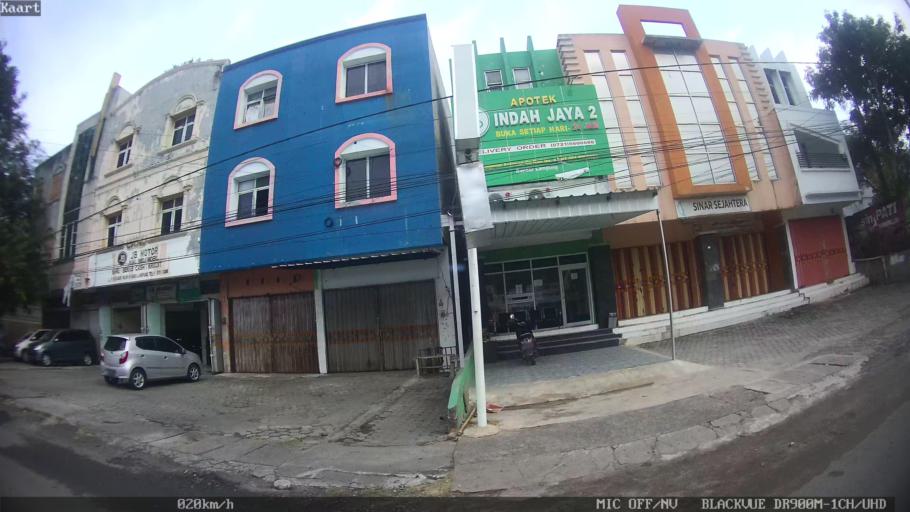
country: ID
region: Lampung
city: Kedaton
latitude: -5.4008
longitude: 105.2855
